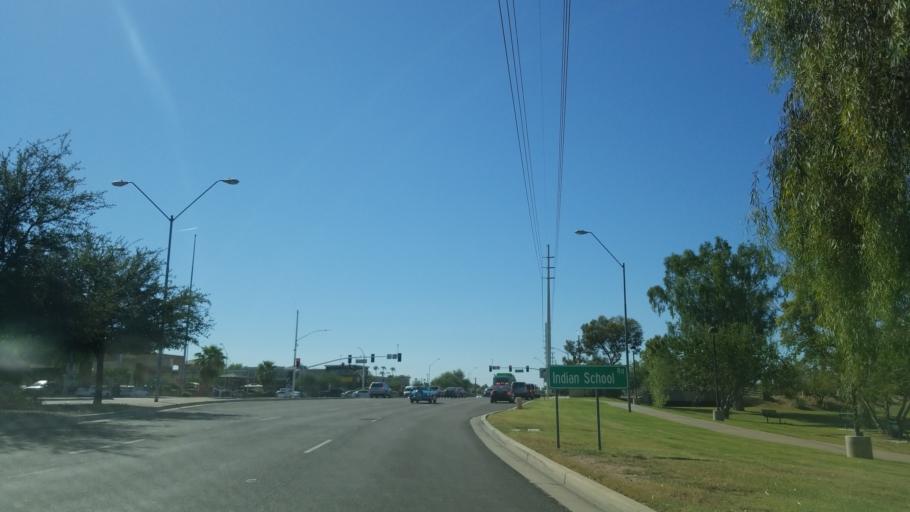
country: US
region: Arizona
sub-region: Maricopa County
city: Scottsdale
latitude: 33.4960
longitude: -111.9091
